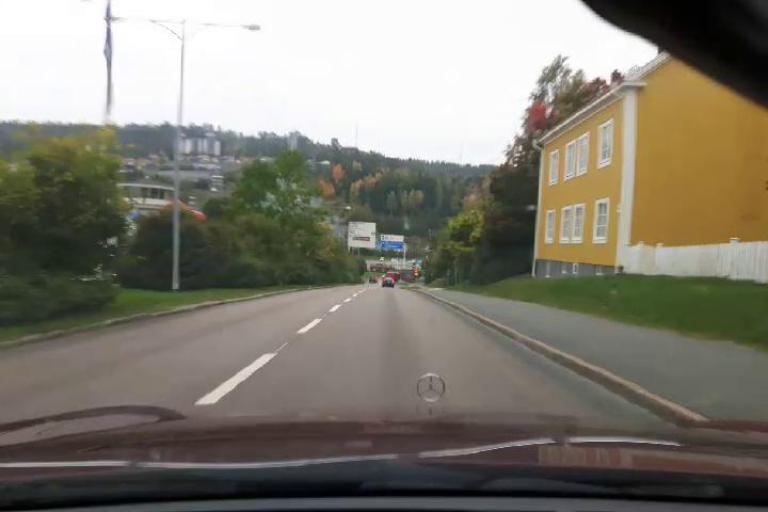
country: SE
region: Vaesternorrland
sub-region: OErnskoeldsviks Kommun
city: Ornskoldsvik
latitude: 63.2906
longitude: 18.7072
